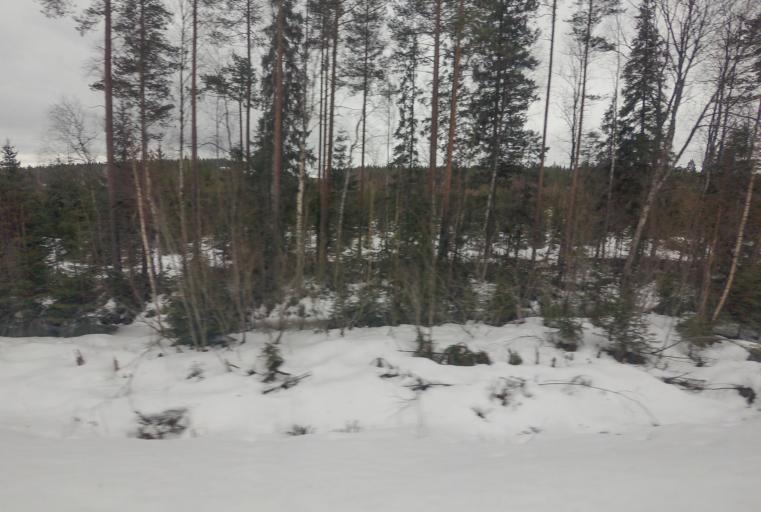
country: FI
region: Southern Savonia
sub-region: Savonlinna
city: Savonlinna
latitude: 61.8685
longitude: 29.0488
